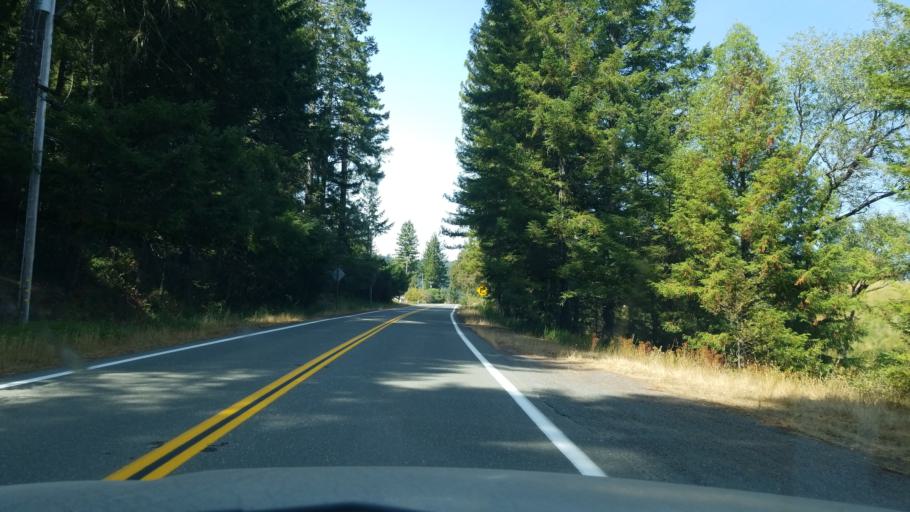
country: US
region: California
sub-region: Mendocino County
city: Laytonville
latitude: 39.8500
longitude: -123.7149
